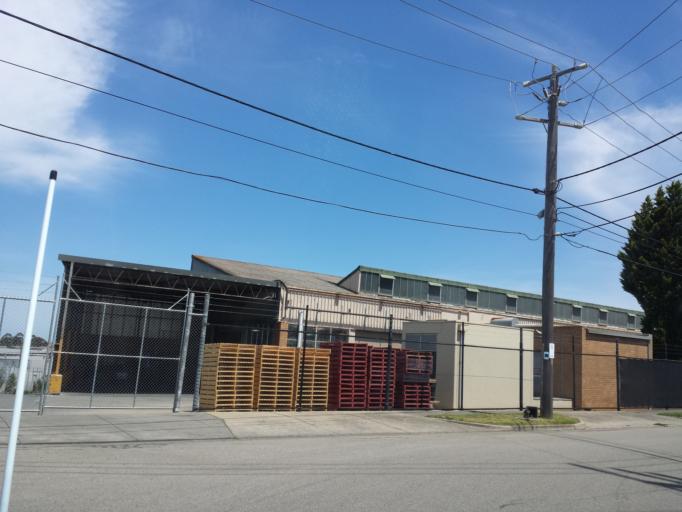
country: AU
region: Victoria
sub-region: Monash
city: Oakleigh South
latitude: -37.9399
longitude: 145.0747
